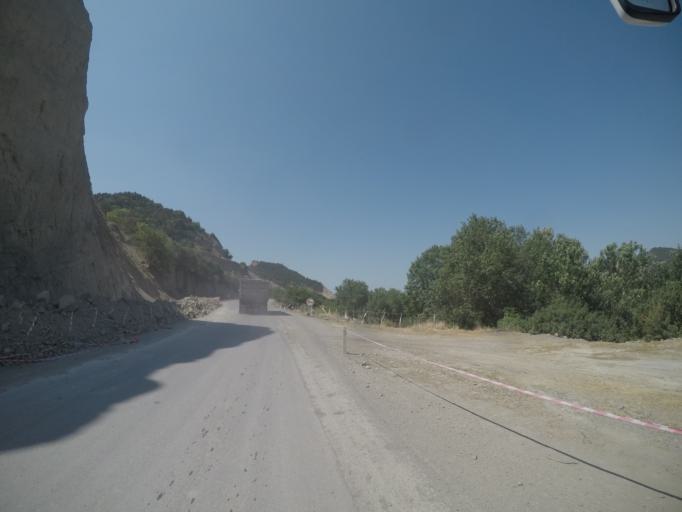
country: AZ
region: Agdas
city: Agdas
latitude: 40.7233
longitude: 47.5640
